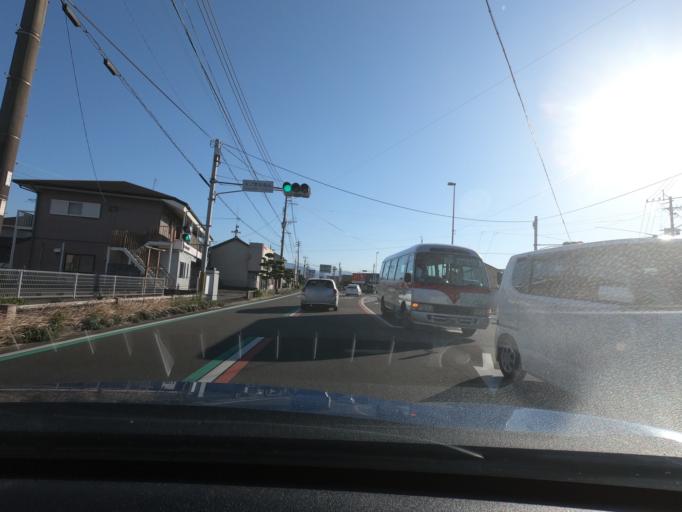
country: JP
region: Kagoshima
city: Izumi
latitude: 32.1177
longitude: 130.3400
